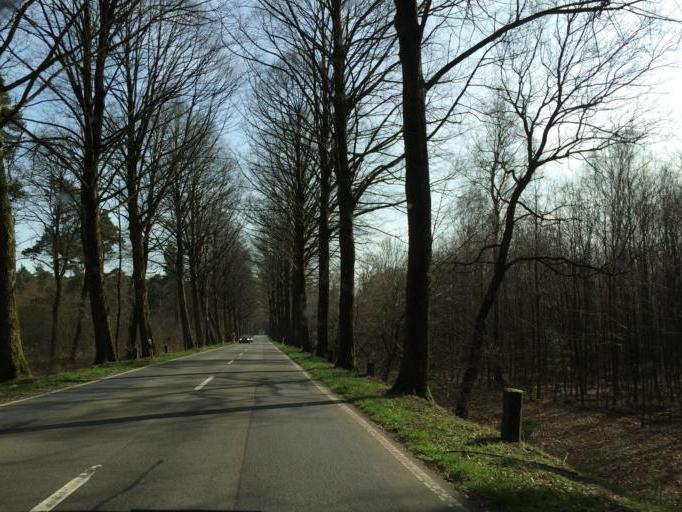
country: DE
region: North Rhine-Westphalia
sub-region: Regierungsbezirk Munster
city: Klein Reken
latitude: 51.7698
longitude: 7.1088
